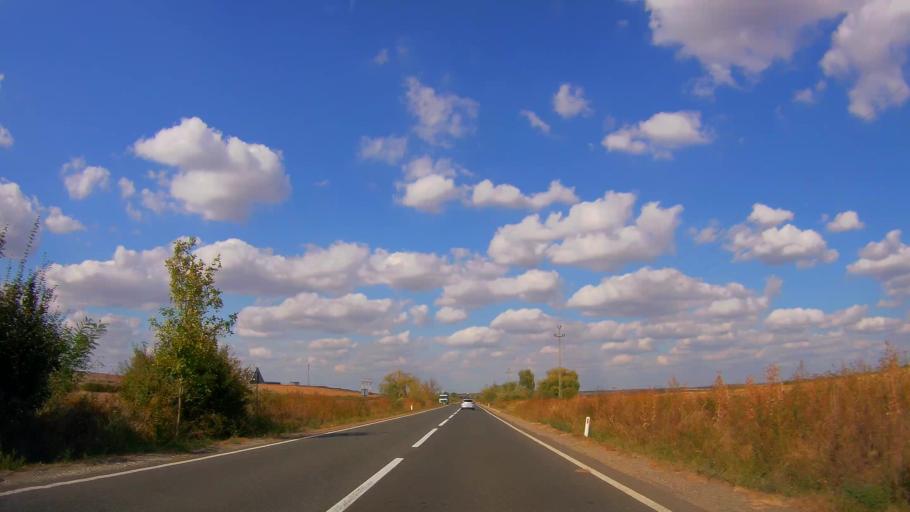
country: RO
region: Satu Mare
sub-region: Oras Ardud
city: Ardud
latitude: 47.5999
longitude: 22.8780
